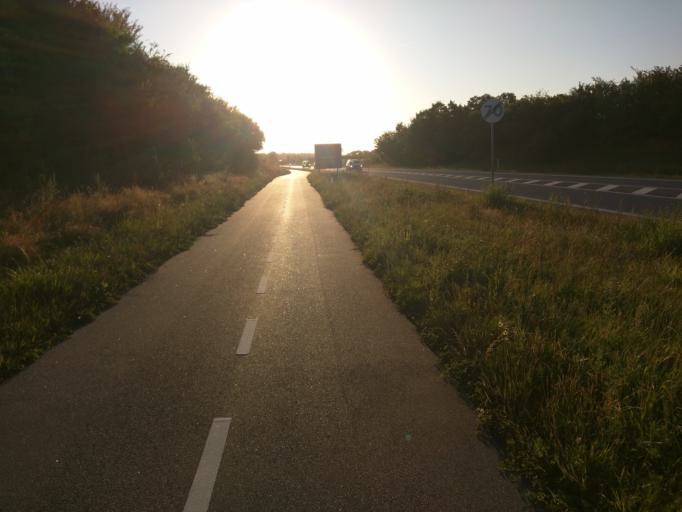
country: DK
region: Central Jutland
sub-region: Viborg Kommune
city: Viborg
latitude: 56.4652
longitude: 9.5049
